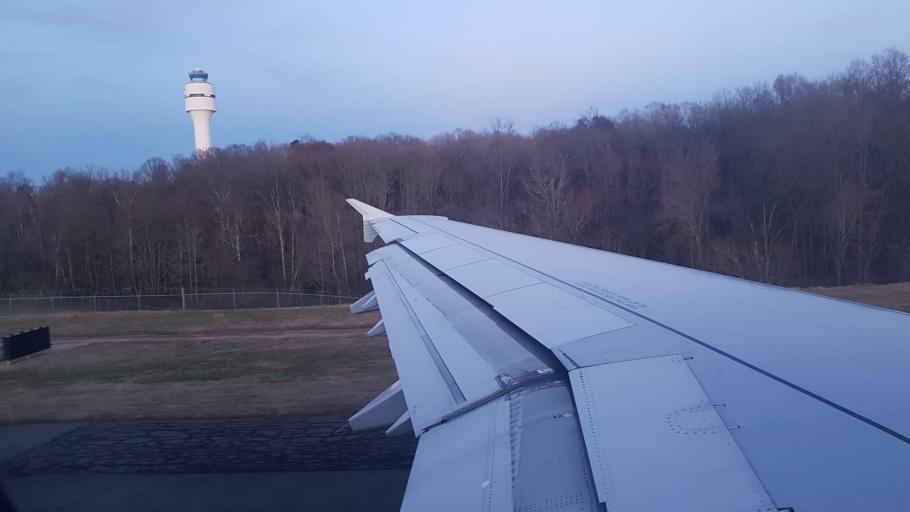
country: US
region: North Carolina
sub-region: Gaston County
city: Belmont
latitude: 35.2015
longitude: -80.9489
